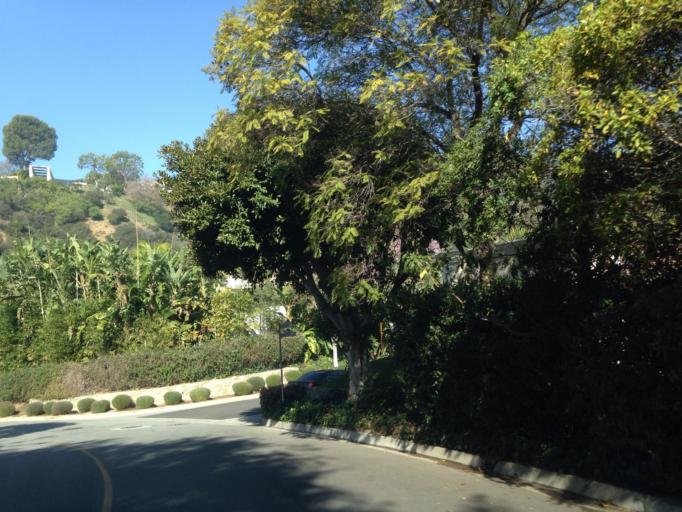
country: US
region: California
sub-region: Los Angeles County
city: Beverly Hills
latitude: 34.1013
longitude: -118.3924
